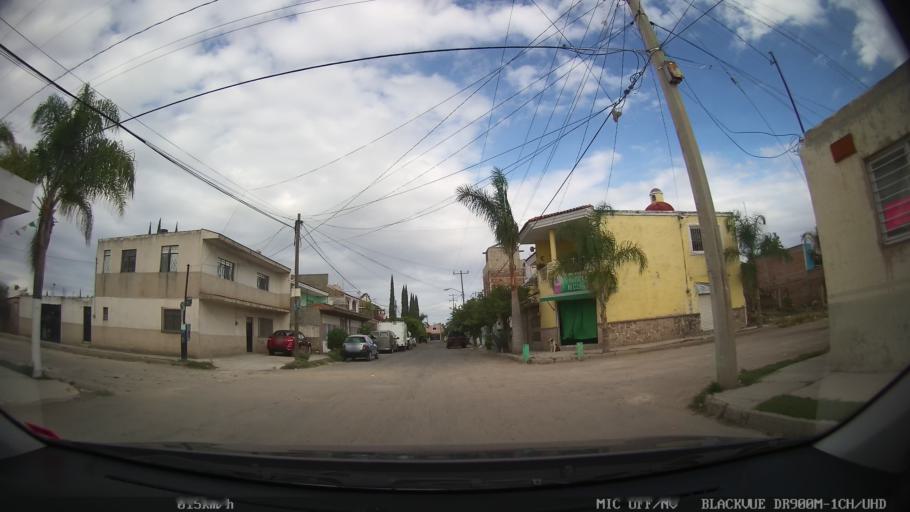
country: MX
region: Jalisco
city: Tonala
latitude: 20.6647
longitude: -103.2356
